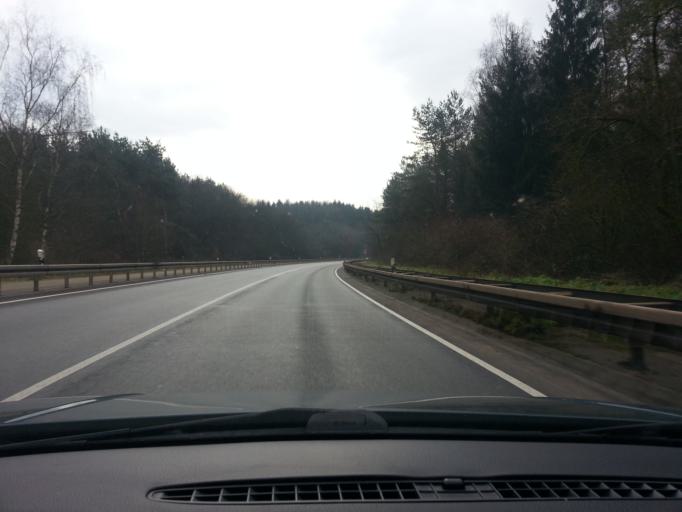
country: DE
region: Saarland
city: Bexbach
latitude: 49.3299
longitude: 7.2342
